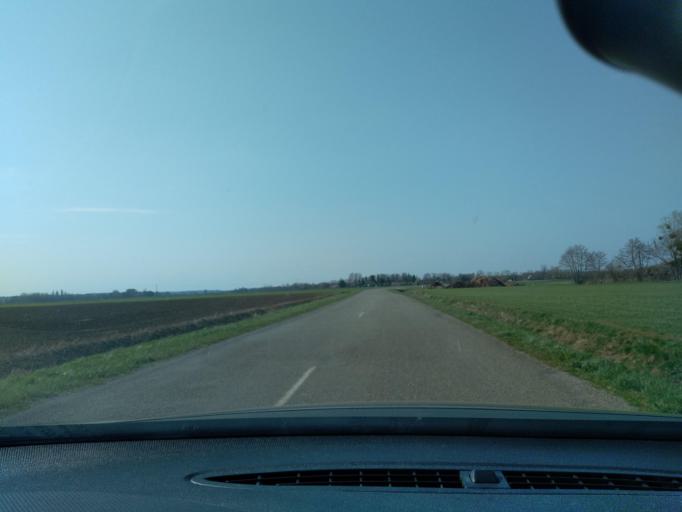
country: FR
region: Franche-Comte
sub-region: Departement du Jura
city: Mont-sous-Vaudrey
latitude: 46.9988
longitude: 5.6023
